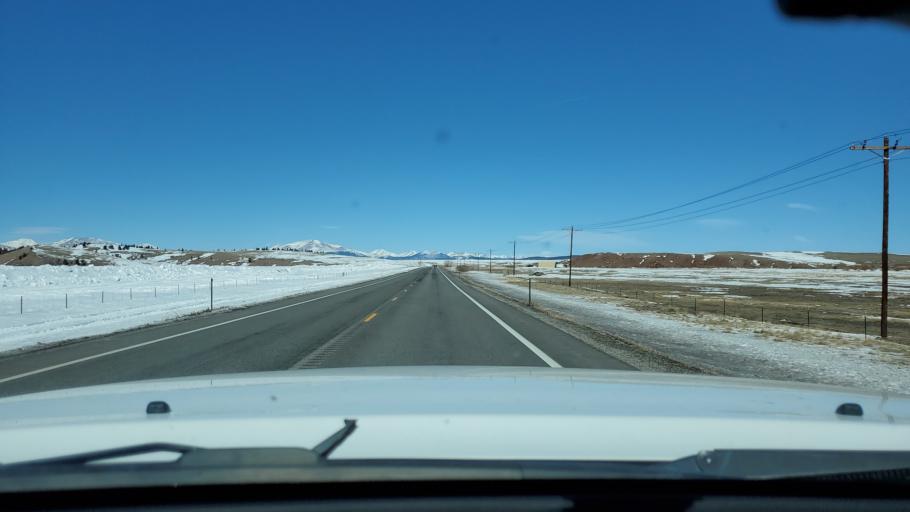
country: US
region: Colorado
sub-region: Park County
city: Fairplay
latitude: 39.0598
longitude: -105.9748
